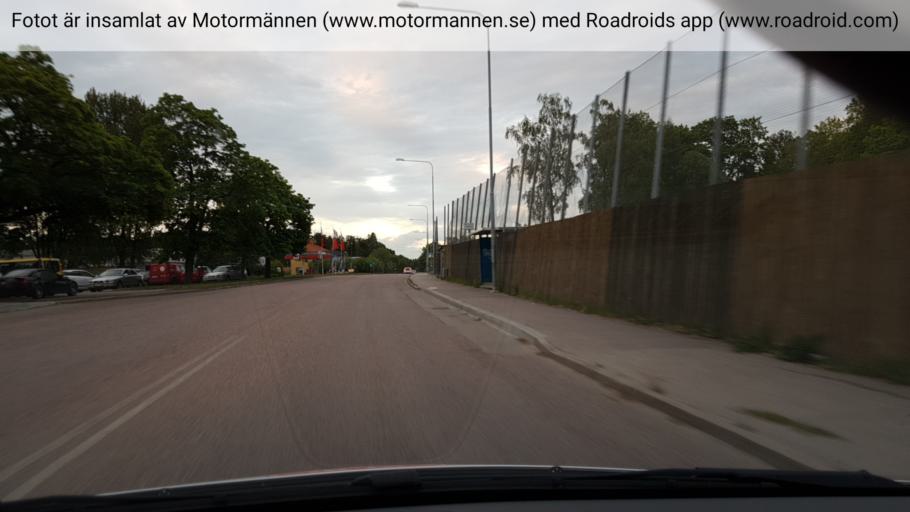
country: SE
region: Vaestmanland
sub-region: Kopings Kommun
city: Koping
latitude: 59.5139
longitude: 16.0033
